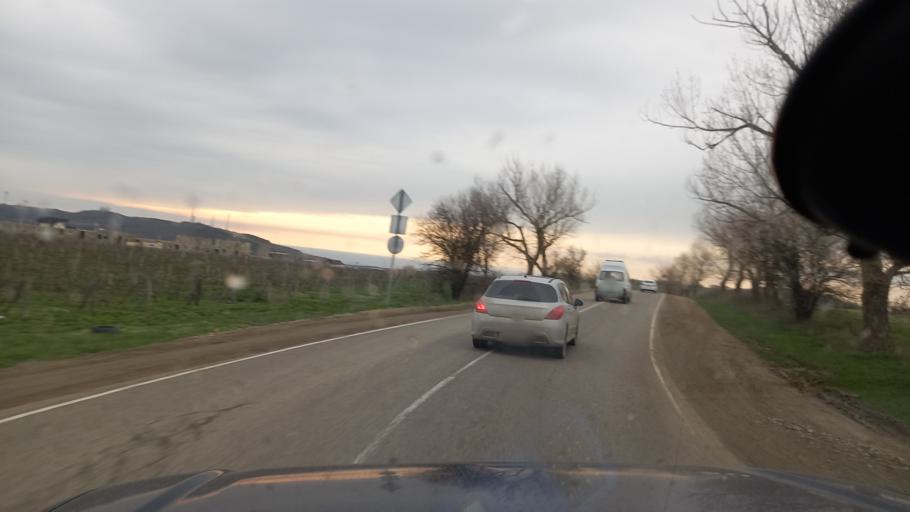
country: RU
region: Krasnodarskiy
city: Sukko
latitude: 44.8392
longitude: 37.3951
